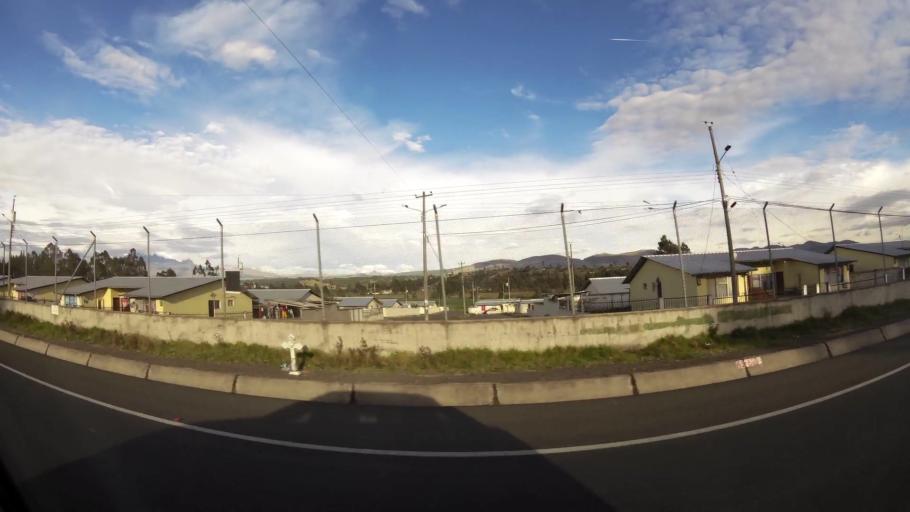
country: EC
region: Cotopaxi
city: Saquisili
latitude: -0.8453
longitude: -78.6193
